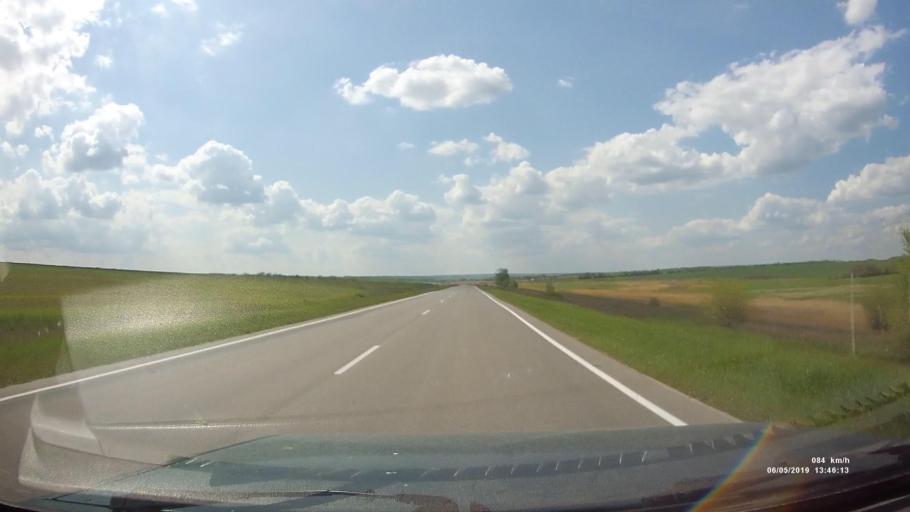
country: RU
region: Rostov
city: Melikhovskaya
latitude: 47.6578
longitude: 40.5860
